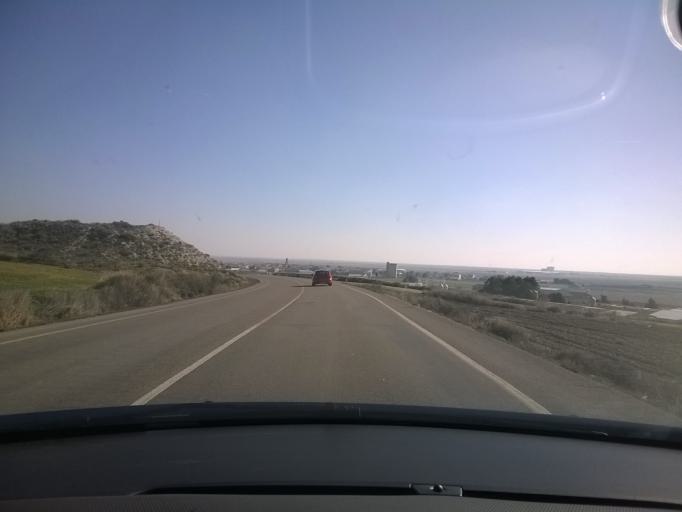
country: ES
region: Aragon
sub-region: Provincia de Zaragoza
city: Bujaraloz
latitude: 41.5076
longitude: -0.1643
